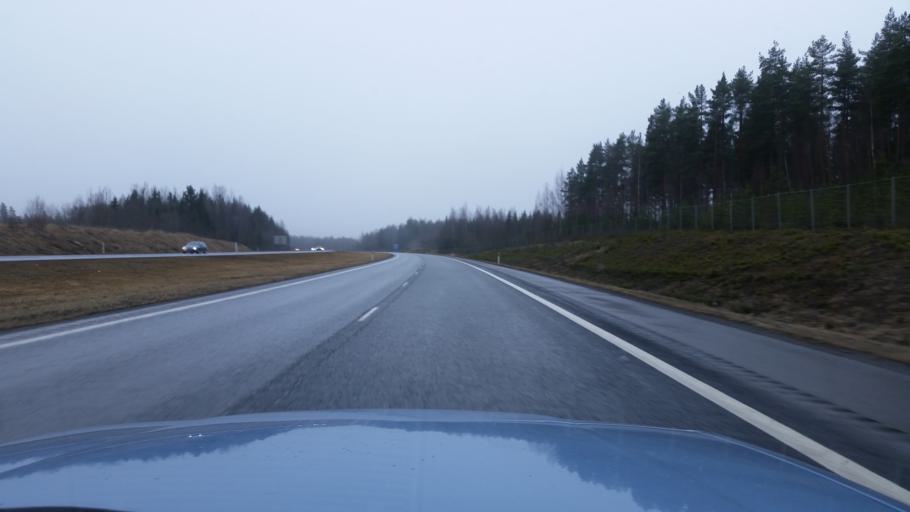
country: FI
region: Pirkanmaa
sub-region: Tampere
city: Lempaeaelae
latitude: 61.2791
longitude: 23.8095
